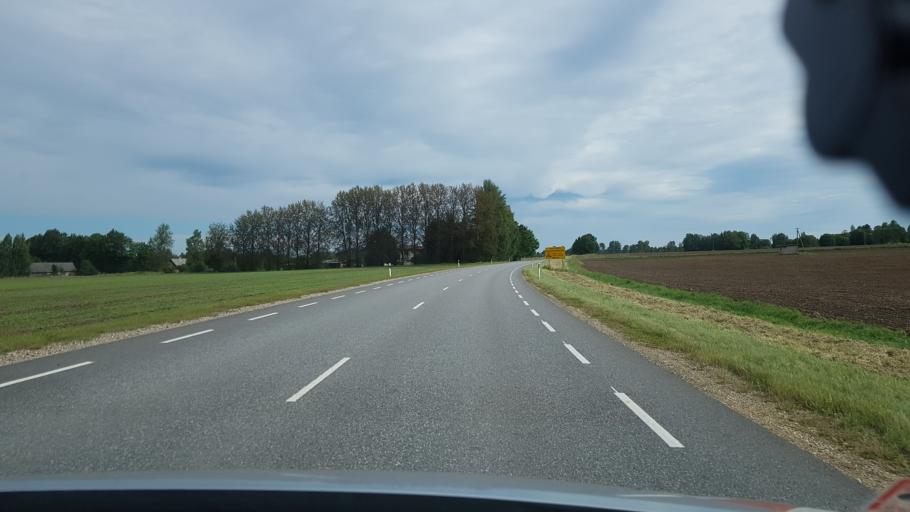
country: EE
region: Viljandimaa
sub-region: Karksi vald
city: Karksi-Nuia
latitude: 58.1741
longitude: 25.5829
